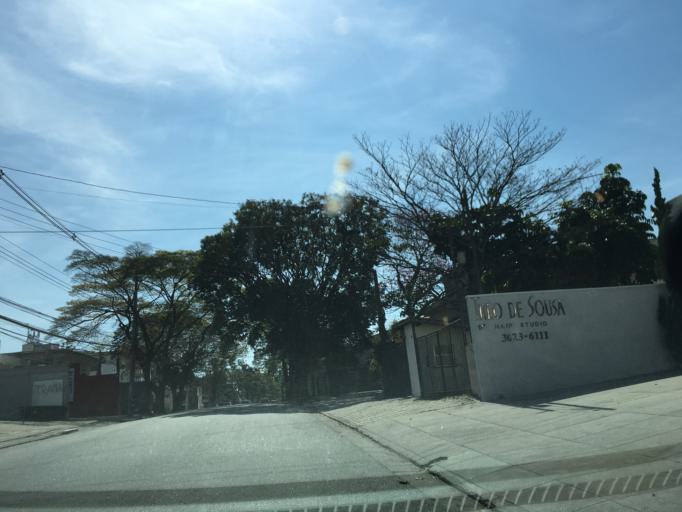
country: BR
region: Sao Paulo
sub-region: Sao Paulo
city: Sao Paulo
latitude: -23.5366
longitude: -46.7130
